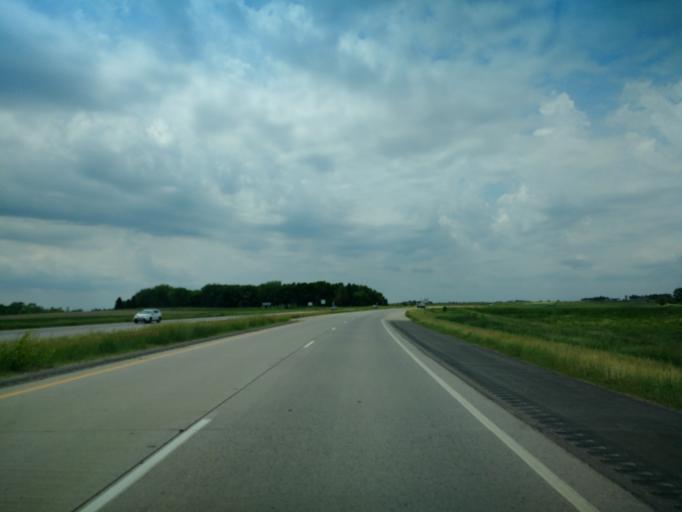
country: US
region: Minnesota
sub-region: Cottonwood County
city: Mountain Lake
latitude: 43.9507
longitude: -94.7961
